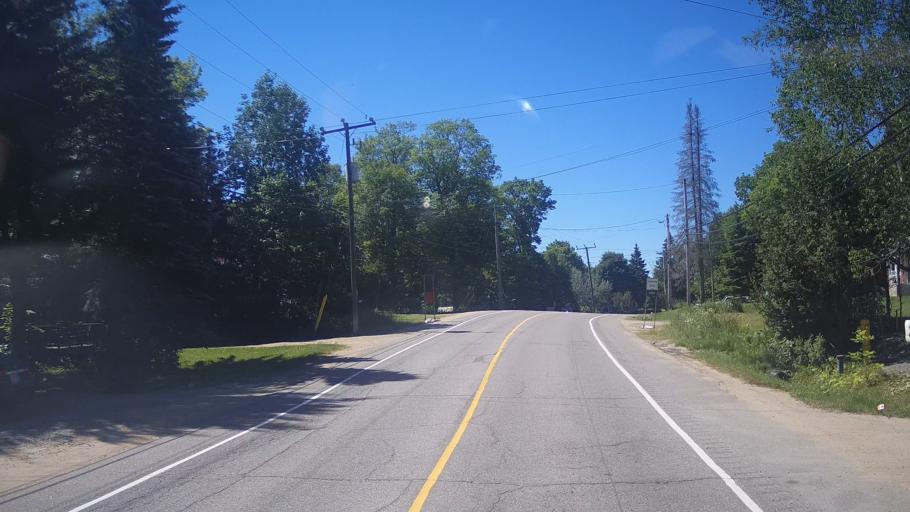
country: CA
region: Ontario
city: Huntsville
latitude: 45.3412
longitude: -79.2013
